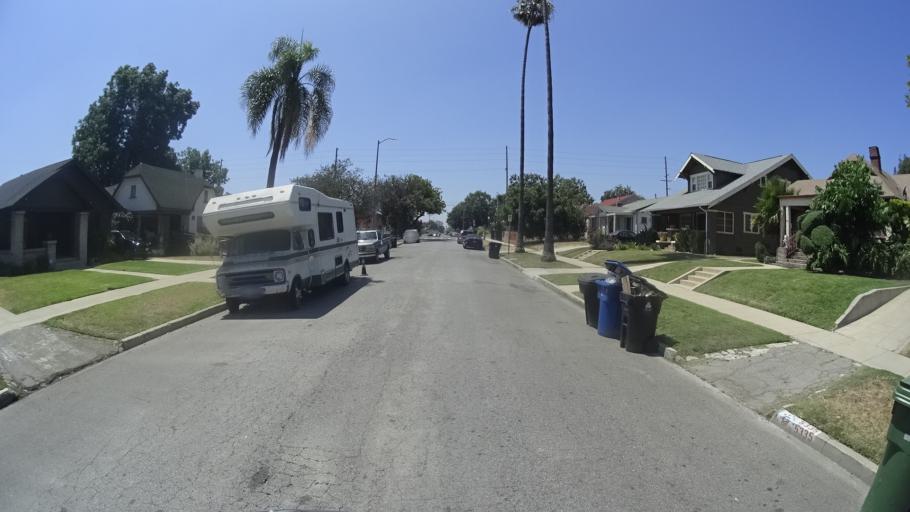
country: US
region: California
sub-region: Los Angeles County
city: View Park-Windsor Hills
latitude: 33.9941
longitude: -118.3258
